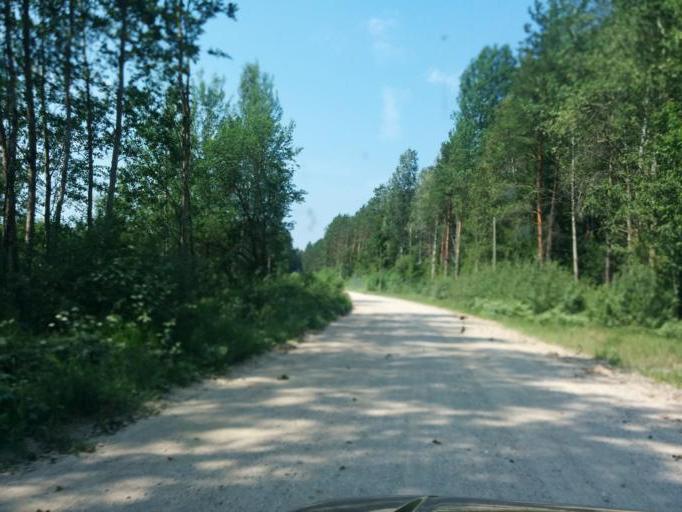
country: LV
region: Baldone
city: Baldone
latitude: 56.7480
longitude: 24.4705
